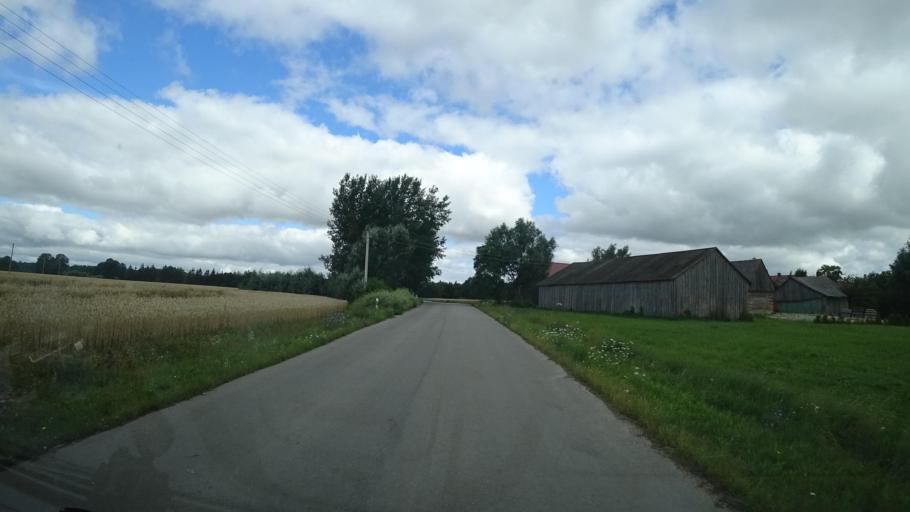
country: LT
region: Marijampoles apskritis
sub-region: Marijampole Municipality
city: Marijampole
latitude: 54.5186
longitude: 23.3231
